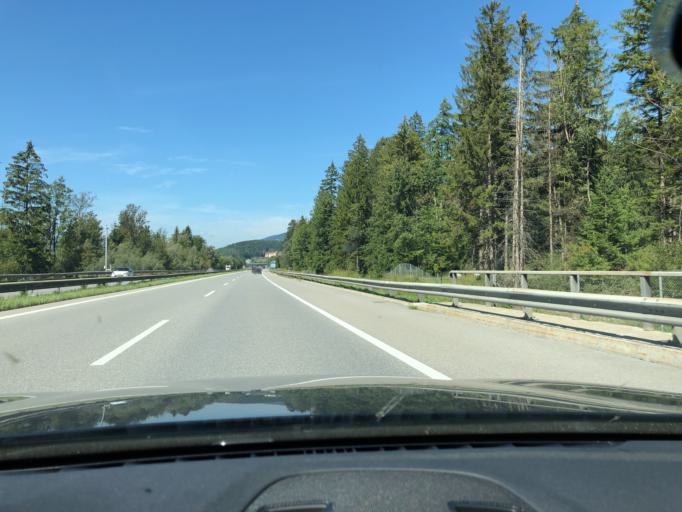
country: AT
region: Vorarlberg
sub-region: Politischer Bezirk Bludenz
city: Bludesch
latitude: 47.1833
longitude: 9.7255
